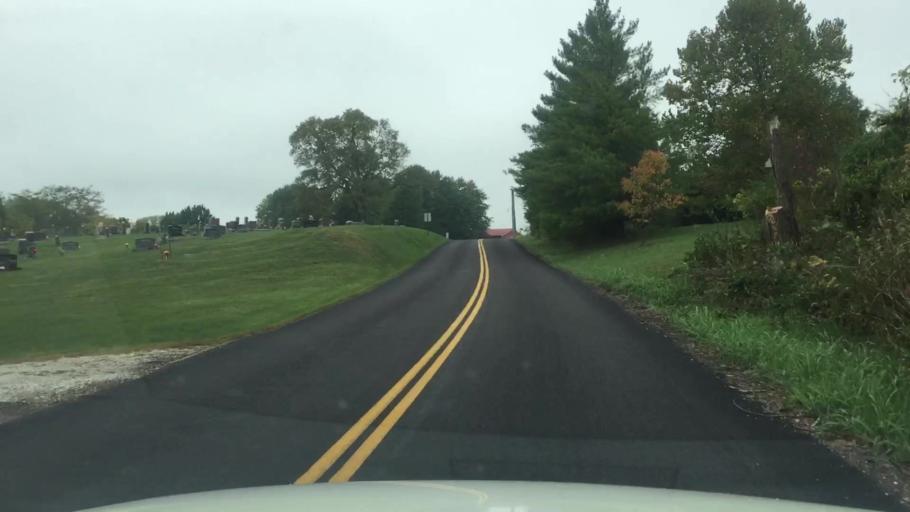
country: US
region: Missouri
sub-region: Boone County
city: Ashland
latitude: 38.8239
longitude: -92.3488
